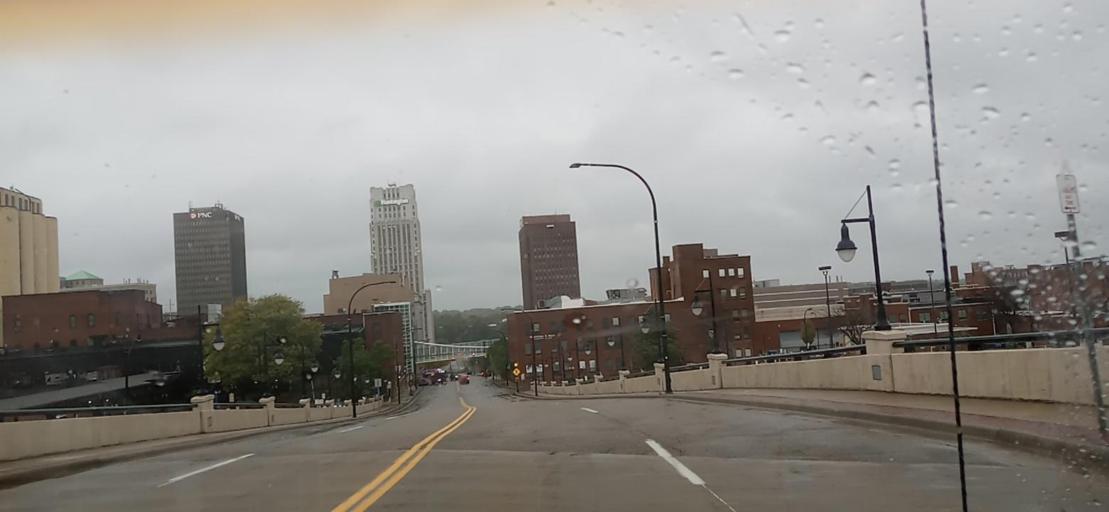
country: US
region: Ohio
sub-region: Summit County
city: Akron
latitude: 41.0813
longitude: -81.5131
